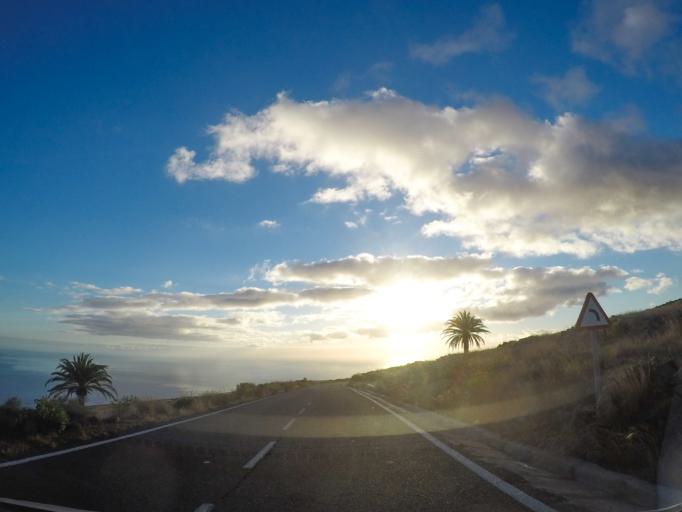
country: ES
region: Canary Islands
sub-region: Provincia de Santa Cruz de Tenerife
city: Alajero
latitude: 28.0464
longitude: -17.2320
